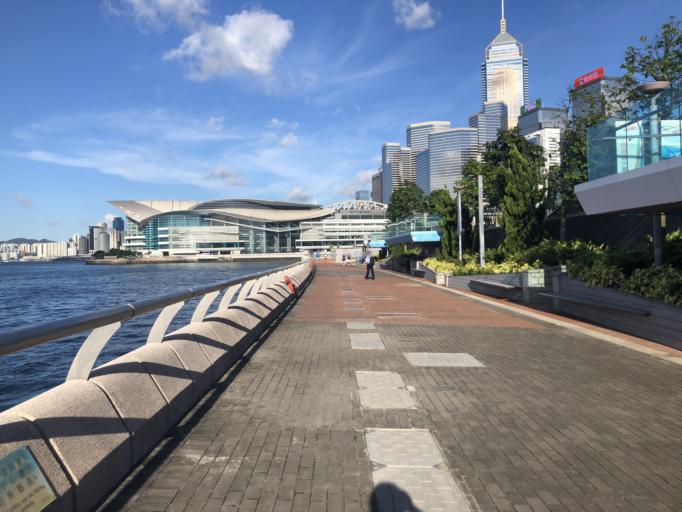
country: HK
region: Wanchai
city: Wan Chai
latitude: 22.2833
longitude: 114.1664
